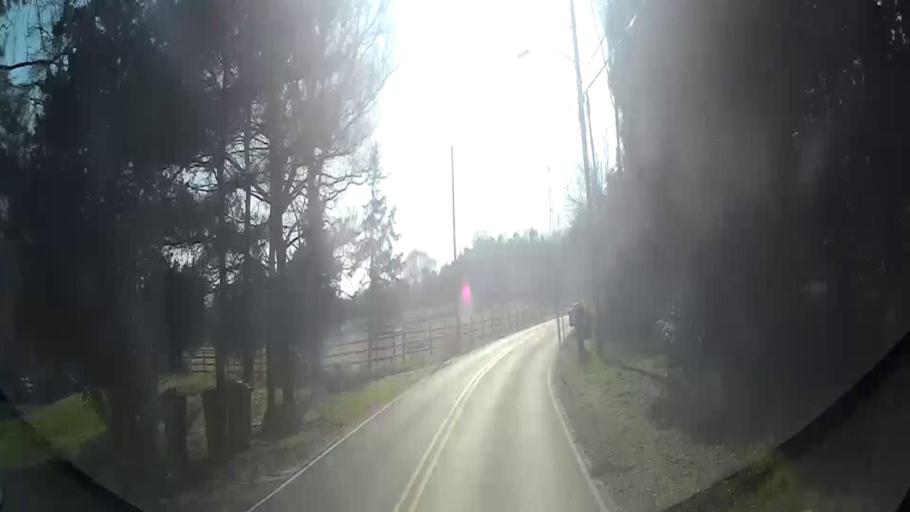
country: US
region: New Jersey
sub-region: Burlington County
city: Marlton
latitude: 39.8528
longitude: -74.9117
